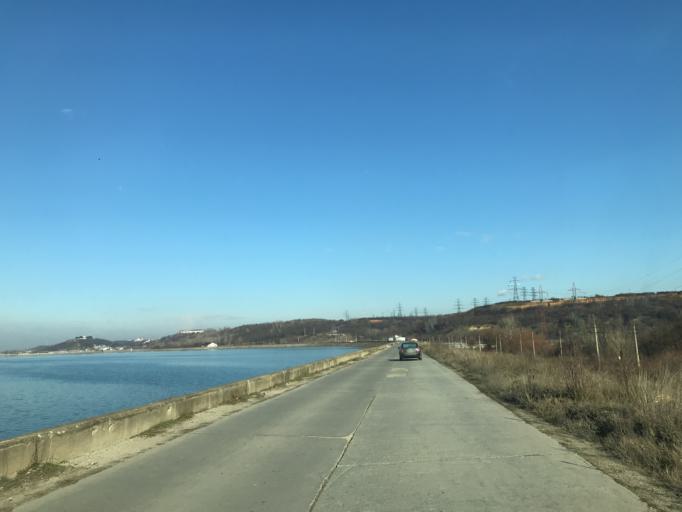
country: RO
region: Olt
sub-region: Municipiul Slatina
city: Slatina
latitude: 44.4001
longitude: 24.3546
